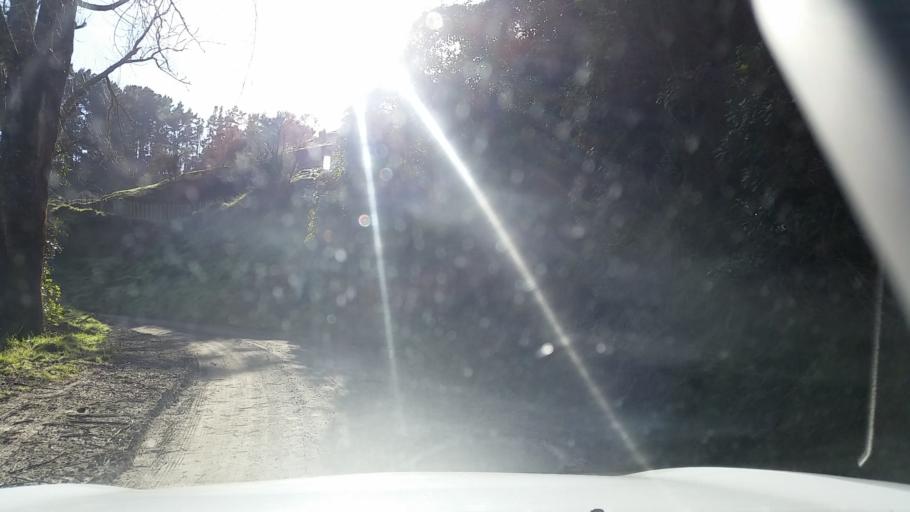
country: NZ
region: Taranaki
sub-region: South Taranaki District
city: Eltham
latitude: -39.5102
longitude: 174.3975
